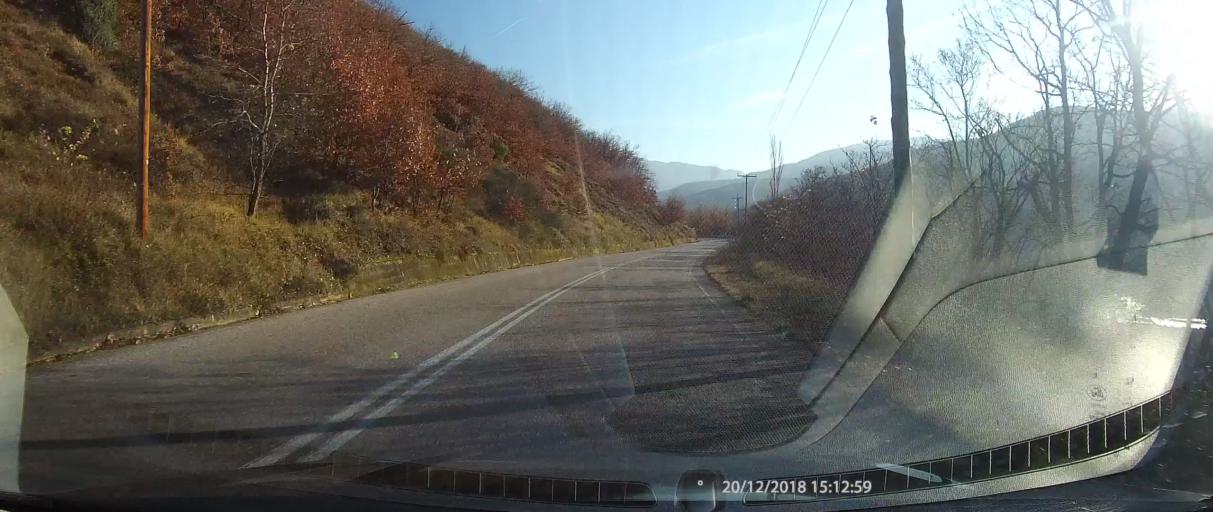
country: GR
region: Central Greece
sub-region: Nomos Fthiotidos
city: Makrakomi
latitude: 38.9376
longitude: 21.9644
